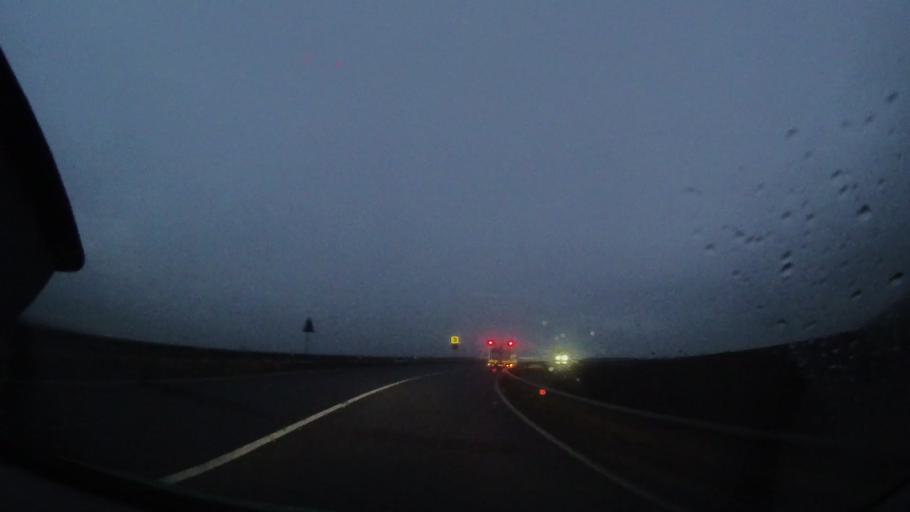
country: RO
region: Harghita
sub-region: Comuna Subcetate
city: Subcetate
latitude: 46.8404
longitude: 25.4762
